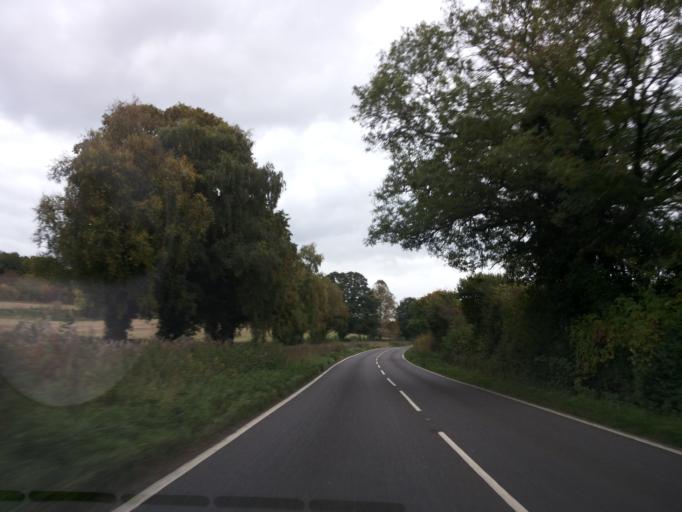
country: GB
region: England
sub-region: Buckinghamshire
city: Great Missenden
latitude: 51.6846
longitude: -0.6744
